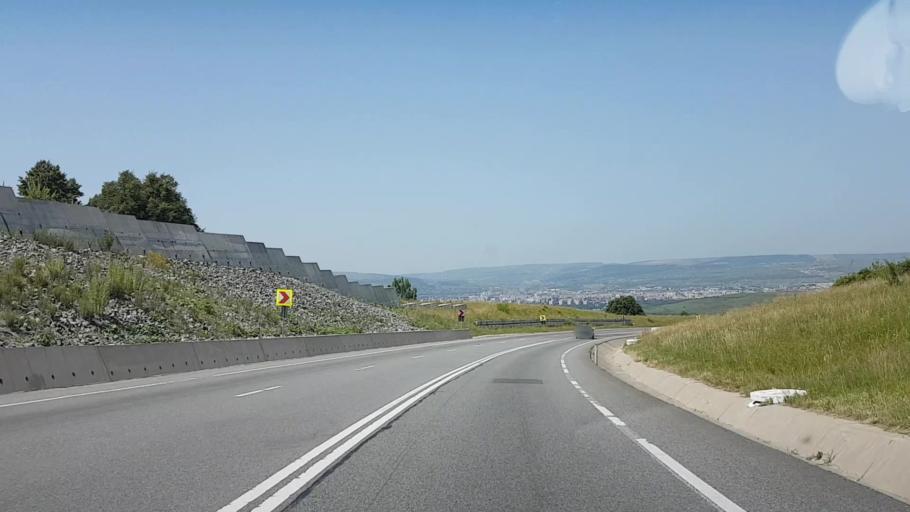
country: RO
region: Cluj
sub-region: Comuna Feleacu
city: Feleacu
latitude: 46.7235
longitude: 23.6459
